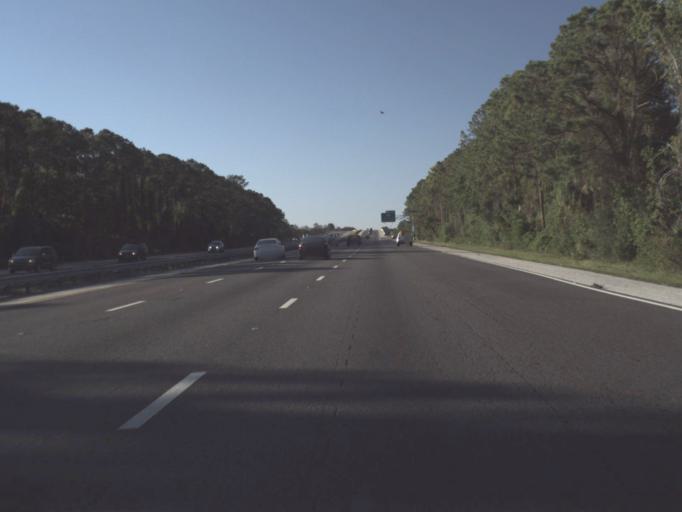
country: US
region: Florida
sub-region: Flagler County
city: Flagler Beach
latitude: 29.4674
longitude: -81.1804
